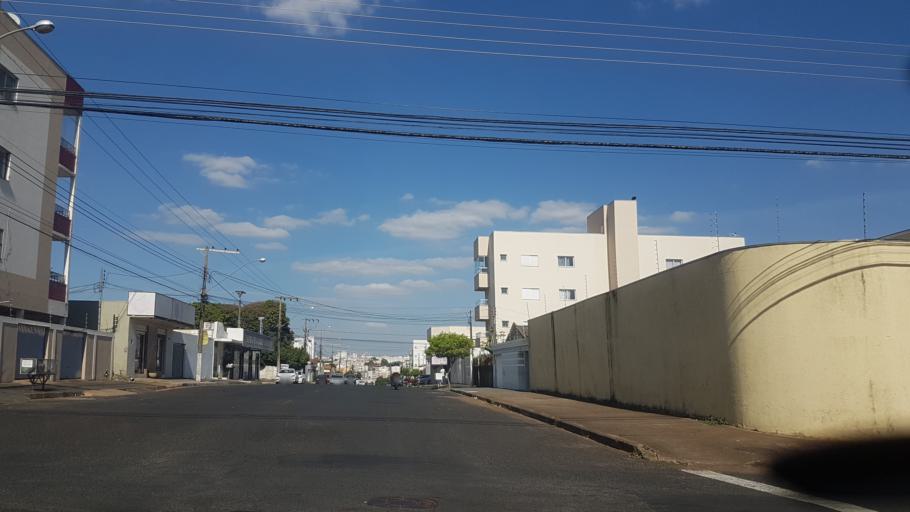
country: BR
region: Minas Gerais
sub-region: Uberlandia
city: Uberlandia
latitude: -18.9049
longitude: -48.2549
